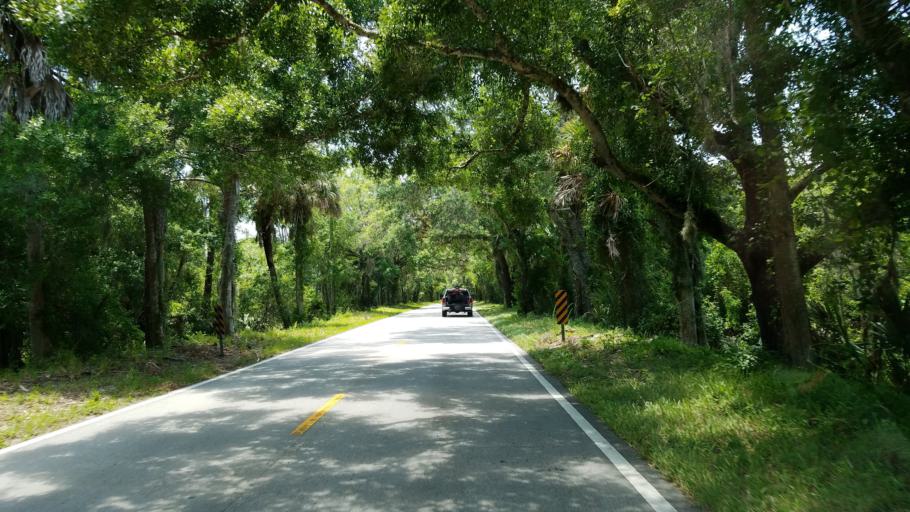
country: US
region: Florida
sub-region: Martin County
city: Indiantown
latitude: 27.1621
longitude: -80.6001
